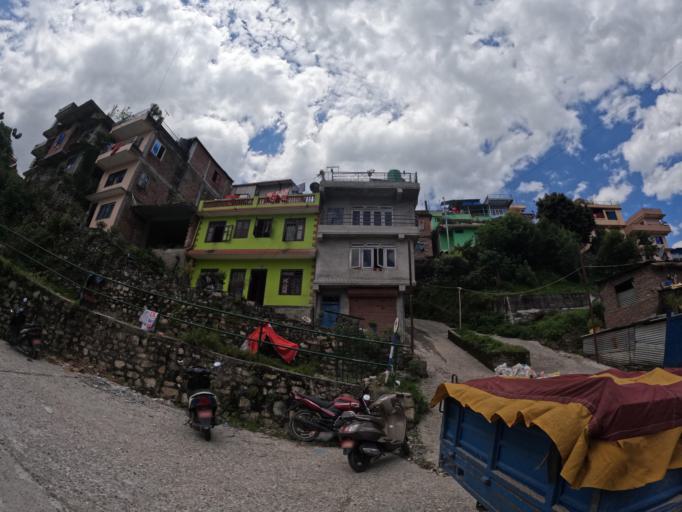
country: NP
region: Central Region
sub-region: Bagmati Zone
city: Kathmandu
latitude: 27.7696
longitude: 85.3293
